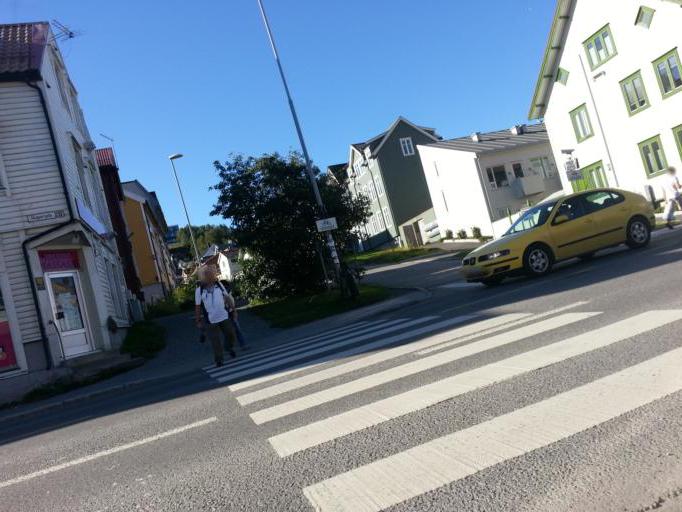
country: NO
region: Troms
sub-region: Tromso
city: Tromso
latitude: 69.6531
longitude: 18.9620
